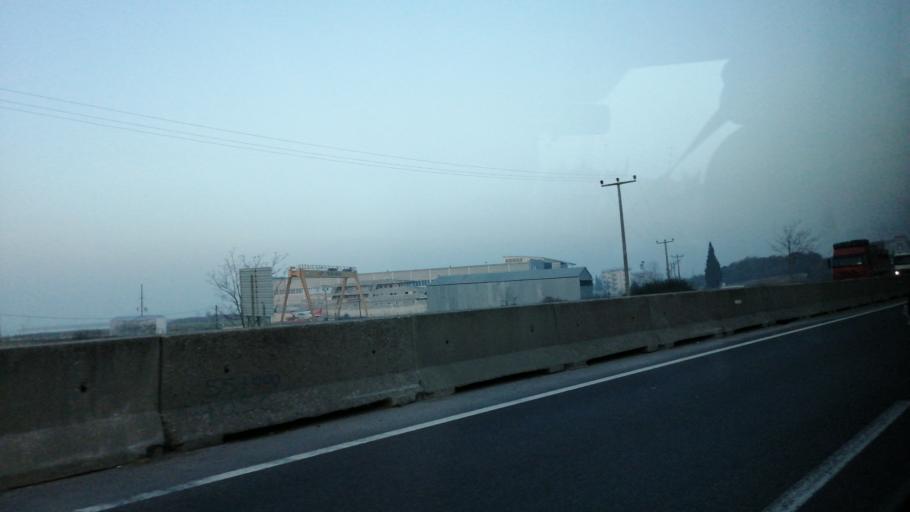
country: TR
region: Yalova
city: Taskopru
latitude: 40.6870
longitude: 29.4362
